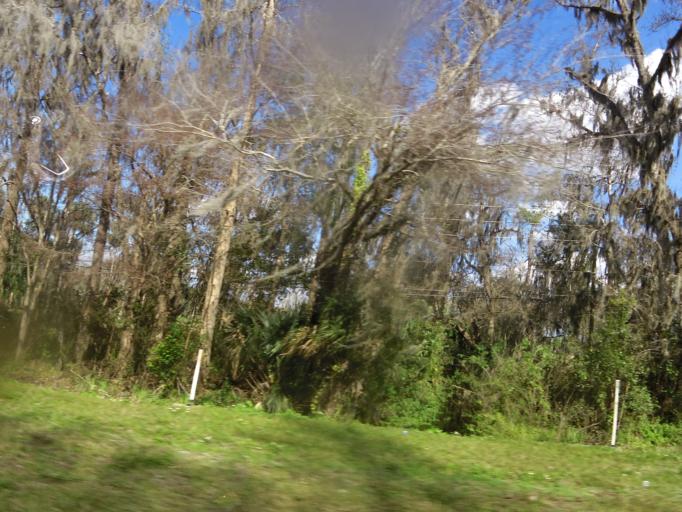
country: US
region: Florida
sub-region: Volusia County
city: De Leon Springs
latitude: 29.1521
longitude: -81.3763
